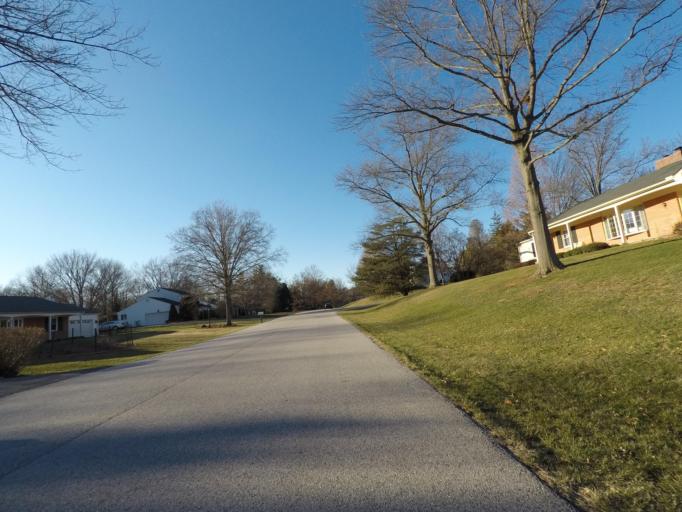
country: US
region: Maryland
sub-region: Howard County
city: Columbia
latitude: 39.2615
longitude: -76.8355
